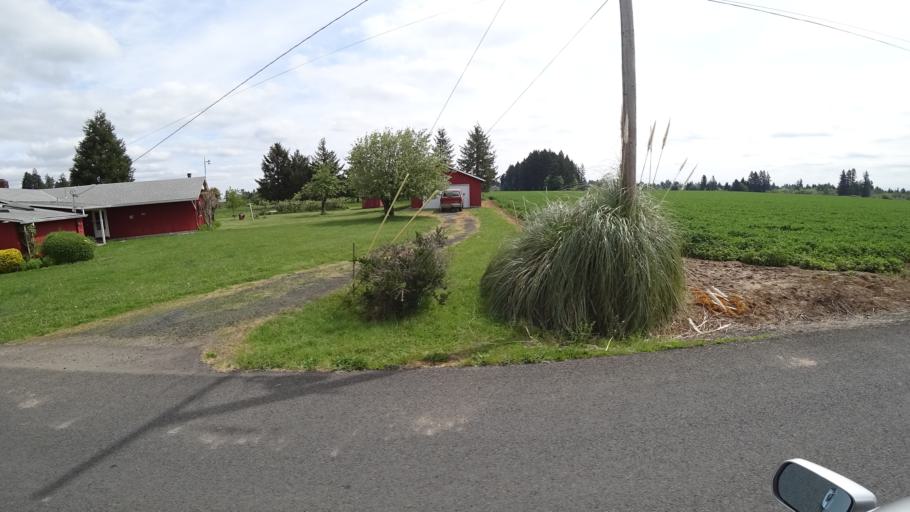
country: US
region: Oregon
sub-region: Washington County
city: Hillsboro
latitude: 45.5390
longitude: -123.0107
